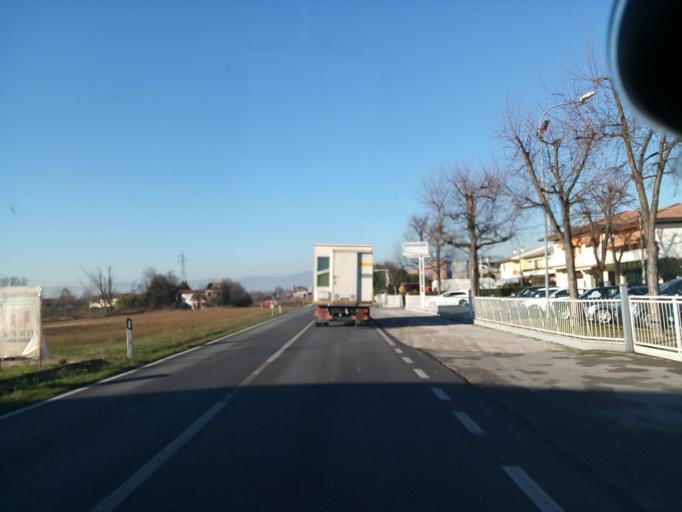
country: IT
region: Veneto
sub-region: Provincia di Treviso
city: Resana
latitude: 45.6413
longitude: 11.9514
